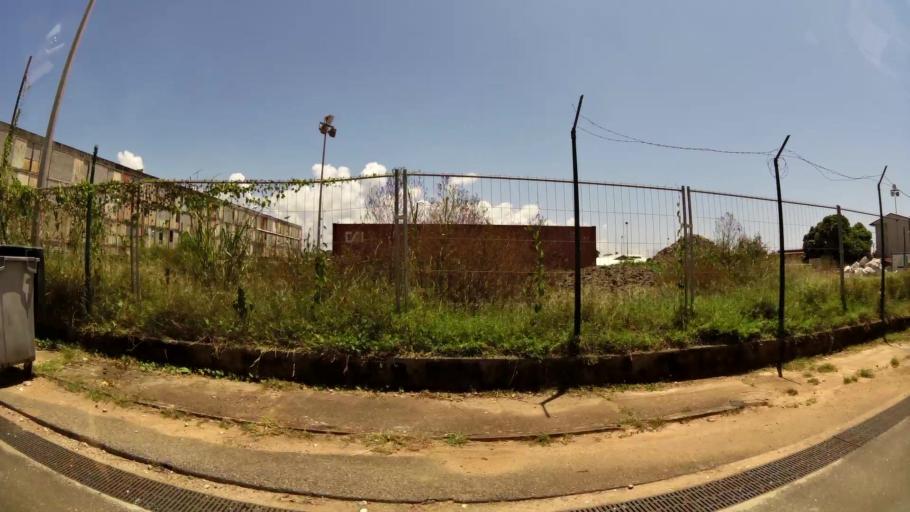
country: GF
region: Guyane
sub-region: Guyane
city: Cayenne
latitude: 4.9328
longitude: -52.3286
